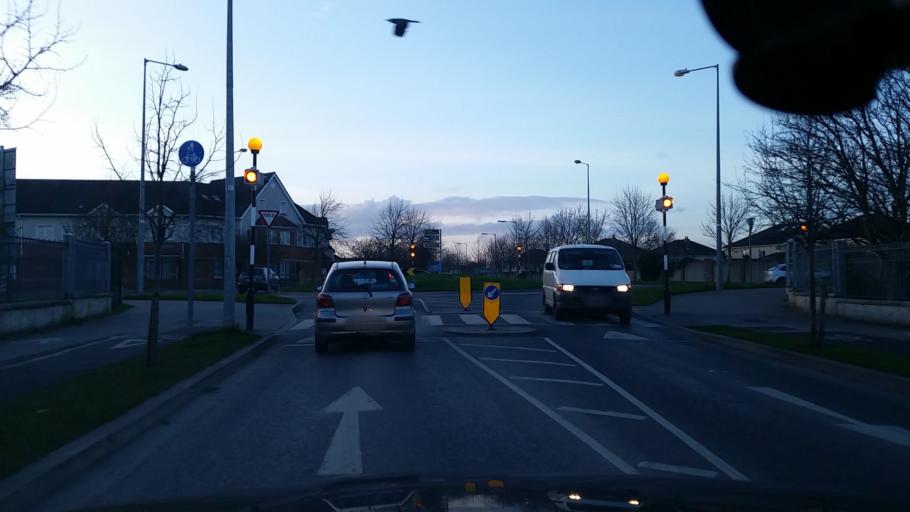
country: IE
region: Leinster
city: Hartstown
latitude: 53.3993
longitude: -6.4323
